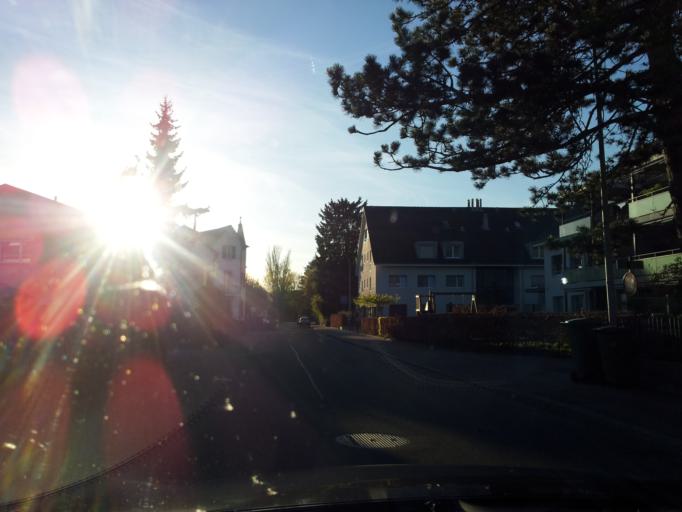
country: CH
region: Aargau
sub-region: Bezirk Baden
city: Neuenhof
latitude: 47.4653
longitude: 8.3331
